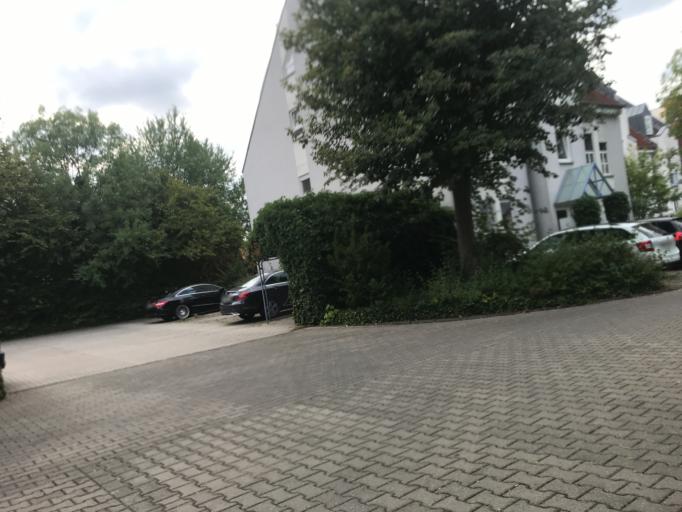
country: DE
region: Rheinland-Pfalz
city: Mainz
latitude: 49.9769
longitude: 8.3039
